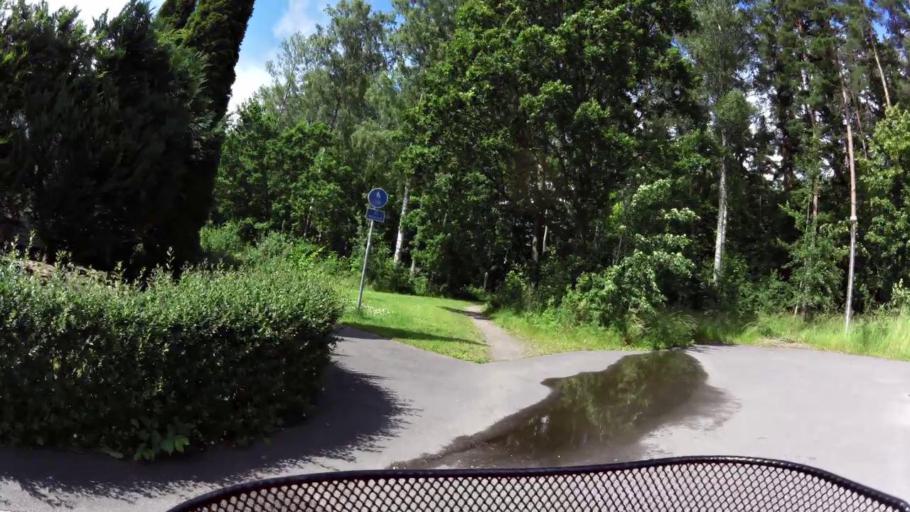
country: SE
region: OEstergoetland
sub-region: Linkopings Kommun
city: Malmslatt
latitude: 58.4207
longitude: 15.5197
